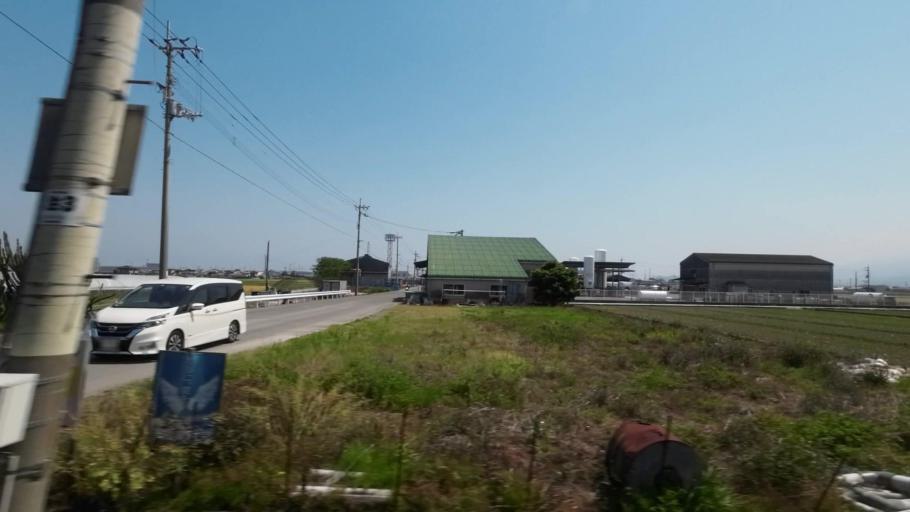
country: JP
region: Ehime
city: Saijo
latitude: 33.9179
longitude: 133.0961
